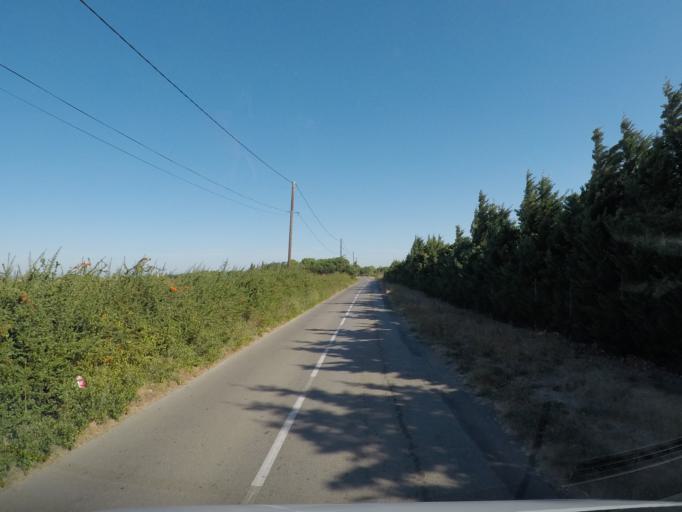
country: FR
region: Languedoc-Roussillon
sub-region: Departement de l'Aude
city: Narbonne
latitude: 43.1503
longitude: 3.0079
